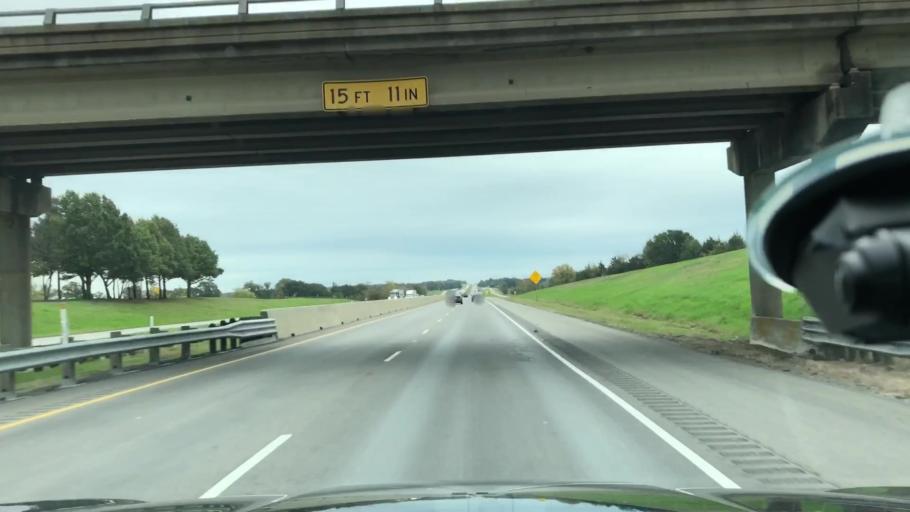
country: US
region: Texas
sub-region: Franklin County
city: Mount Vernon
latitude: 33.1661
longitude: -95.3074
